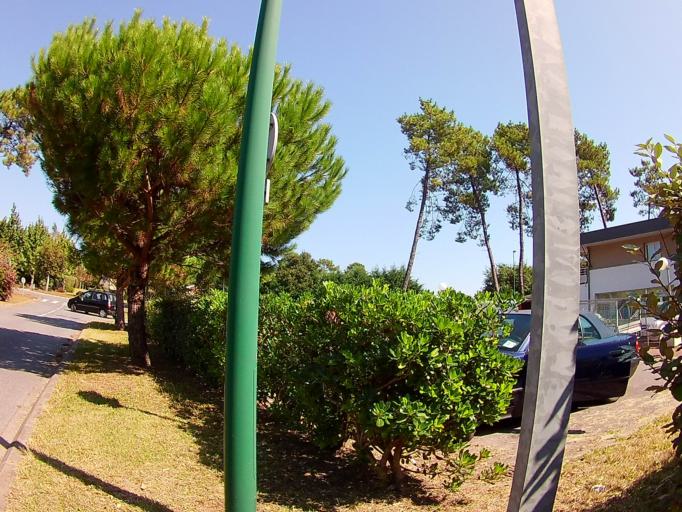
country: FR
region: Aquitaine
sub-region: Departement des Landes
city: Labenne
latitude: 43.5986
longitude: -1.4341
